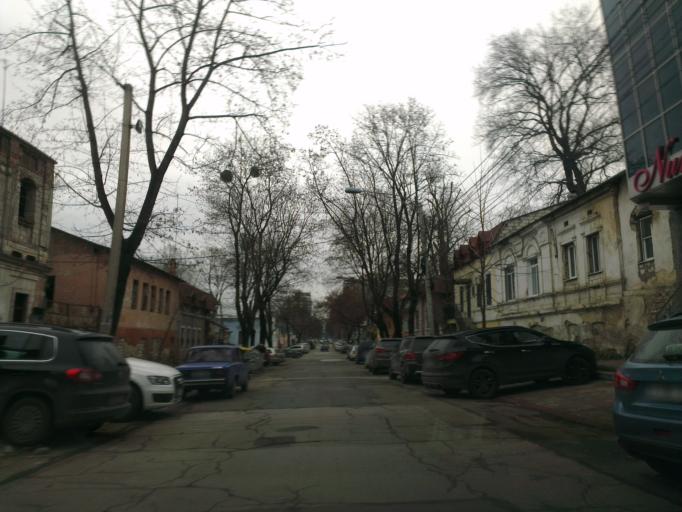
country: MD
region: Chisinau
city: Chisinau
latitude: 47.0302
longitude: 28.8306
